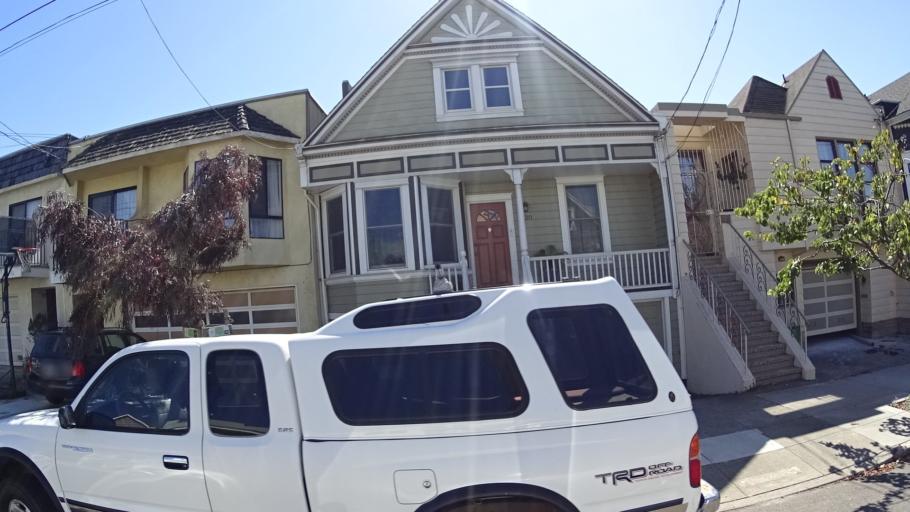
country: US
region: California
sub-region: San Francisco County
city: San Francisco
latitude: 37.7366
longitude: -122.4228
